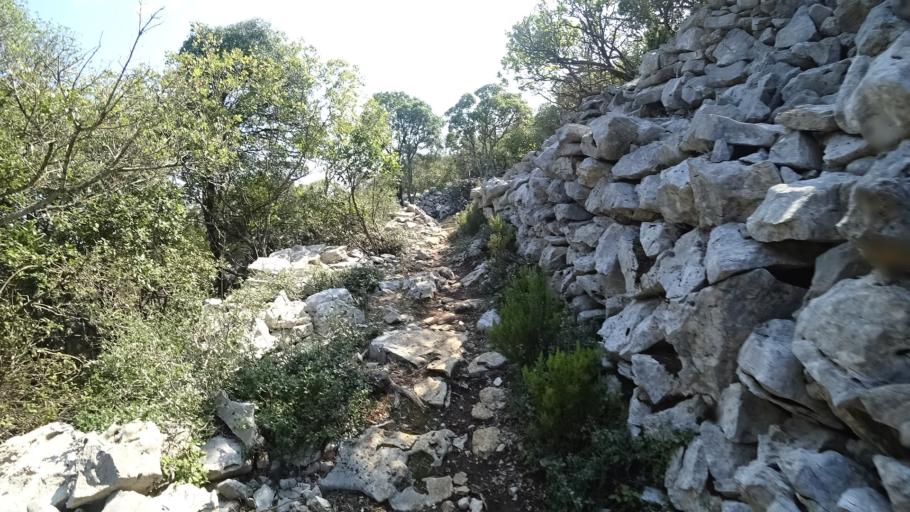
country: HR
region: Primorsko-Goranska
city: Mali Losinj
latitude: 44.4901
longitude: 14.5326
